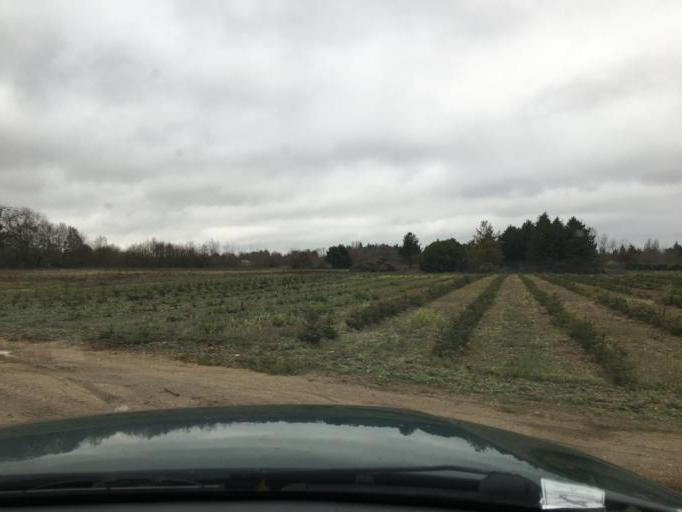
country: FR
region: Centre
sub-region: Departement du Loiret
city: Olivet
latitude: 47.8505
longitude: 1.8793
